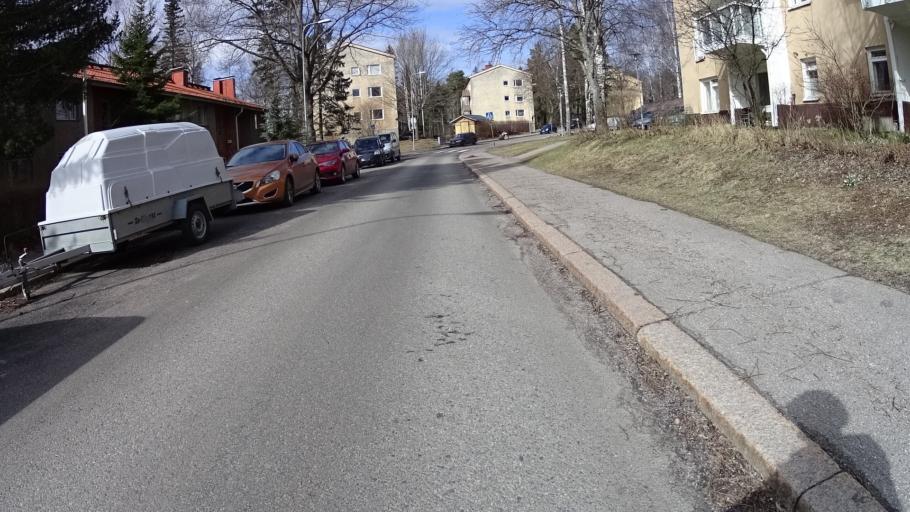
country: FI
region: Uusimaa
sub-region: Helsinki
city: Teekkarikylae
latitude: 60.2263
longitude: 24.8885
